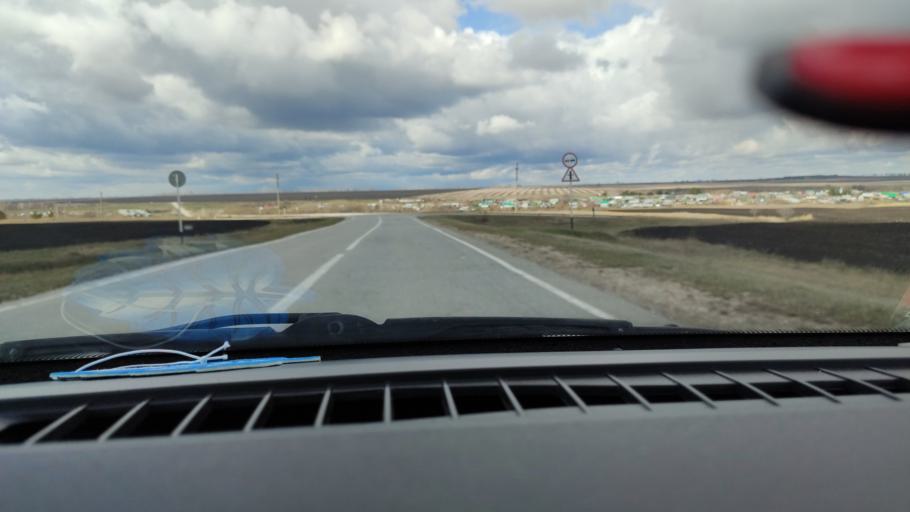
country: RU
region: Samara
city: Novyy Buyan
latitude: 53.7840
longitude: 50.0503
